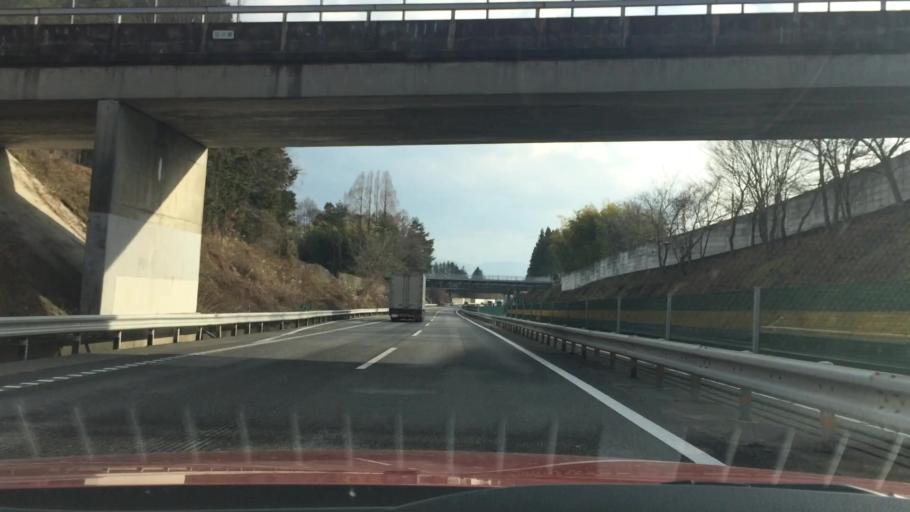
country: JP
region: Nagano
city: Ina
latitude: 35.8111
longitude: 137.9270
